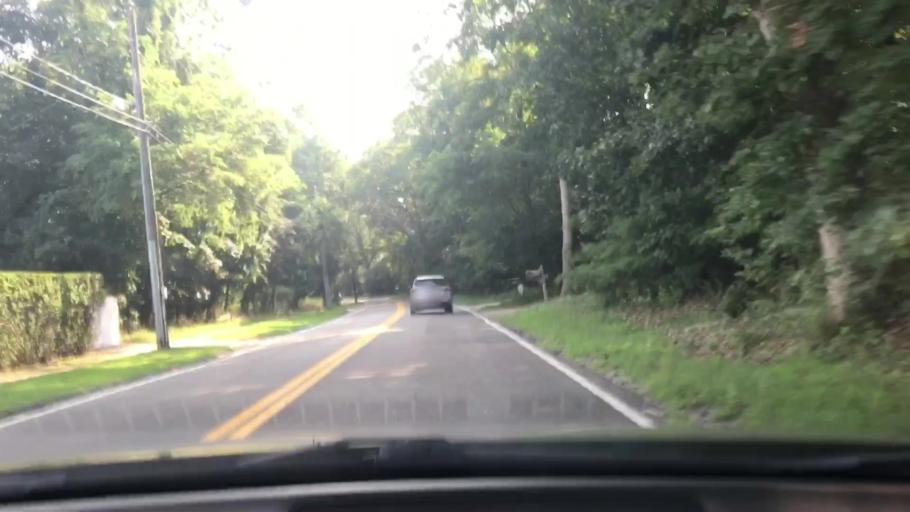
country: US
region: New York
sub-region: Suffolk County
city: Sag Harbor
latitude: 40.9867
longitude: -72.3066
